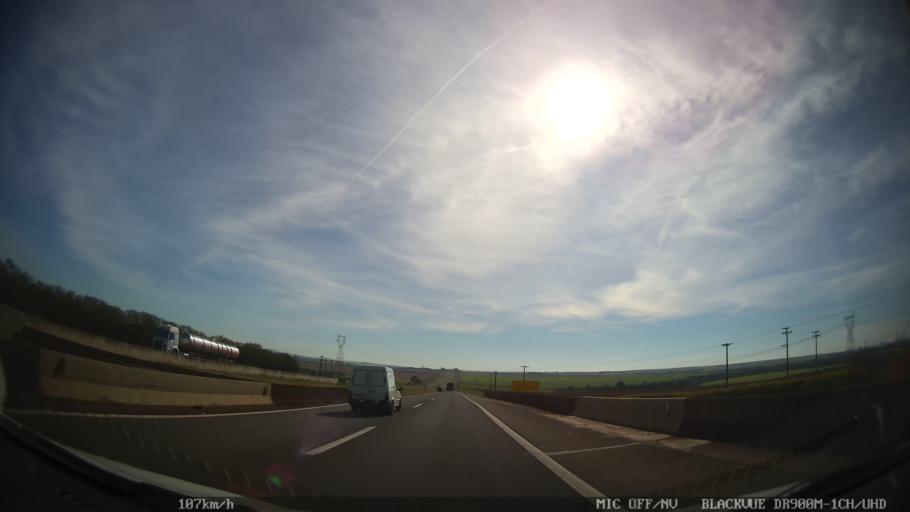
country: BR
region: Sao Paulo
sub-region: Cordeiropolis
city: Cordeiropolis
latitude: -22.4370
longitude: -47.3958
